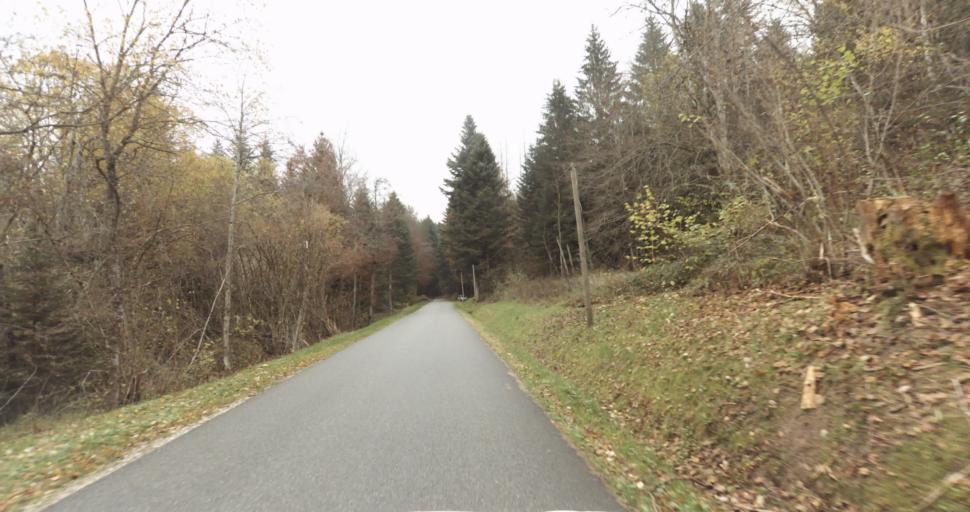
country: FR
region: Rhone-Alpes
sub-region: Departement de la Haute-Savoie
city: Saint-Jorioz
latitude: 45.7625
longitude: 6.1303
